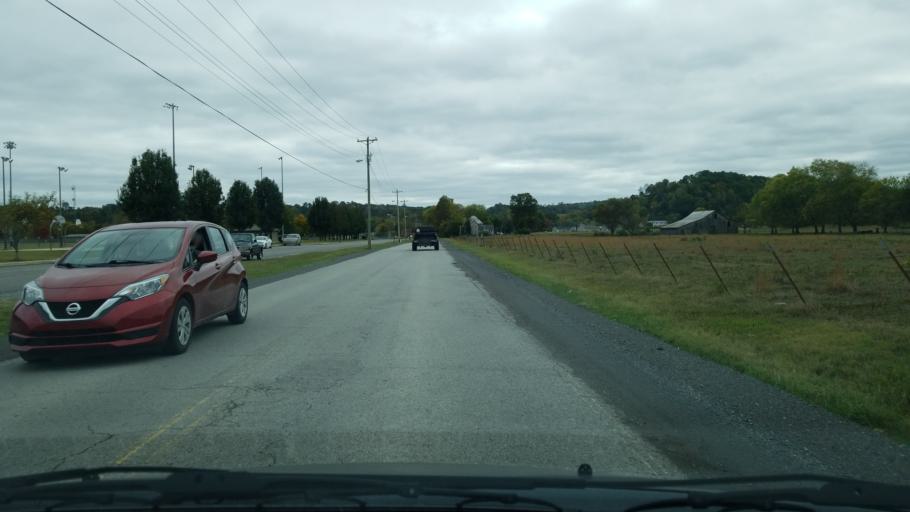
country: US
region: Tennessee
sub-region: Rhea County
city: Dayton
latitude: 35.4961
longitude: -85.0240
